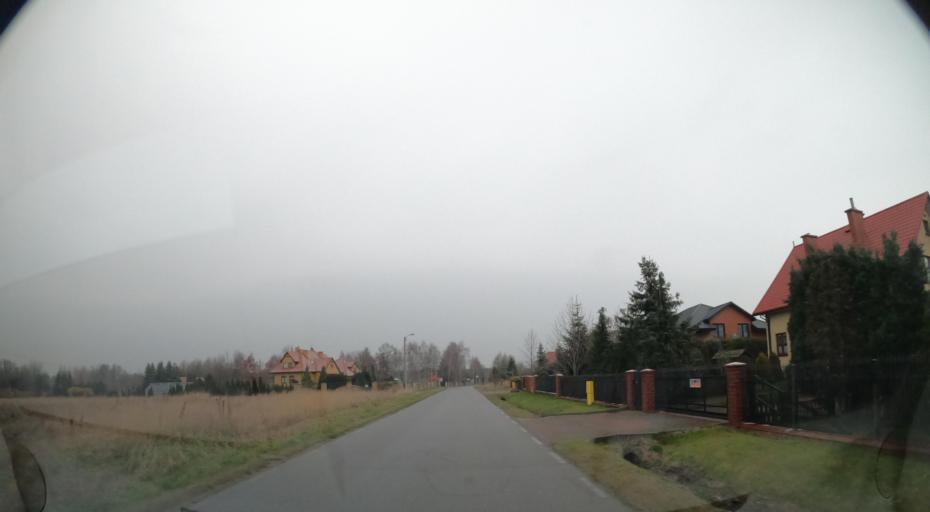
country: PL
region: Masovian Voivodeship
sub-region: Radom
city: Radom
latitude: 51.4183
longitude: 21.2240
